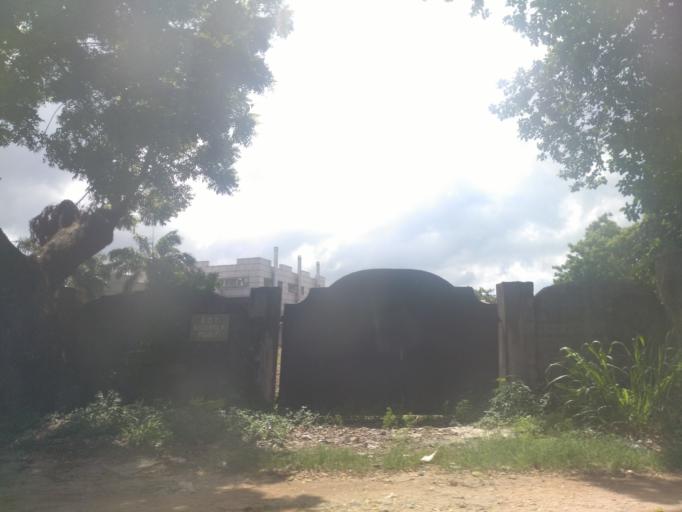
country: TZ
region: Zanzibar Urban/West
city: Zanzibar
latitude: -6.1577
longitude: 39.2030
